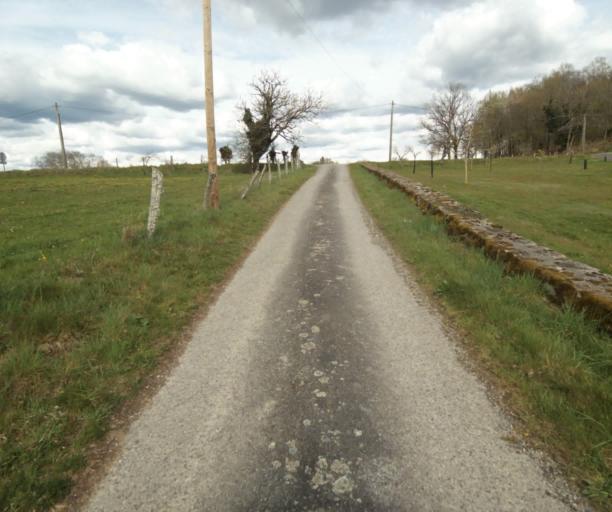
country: FR
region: Limousin
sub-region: Departement de la Correze
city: Argentat
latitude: 45.1868
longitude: 1.9353
